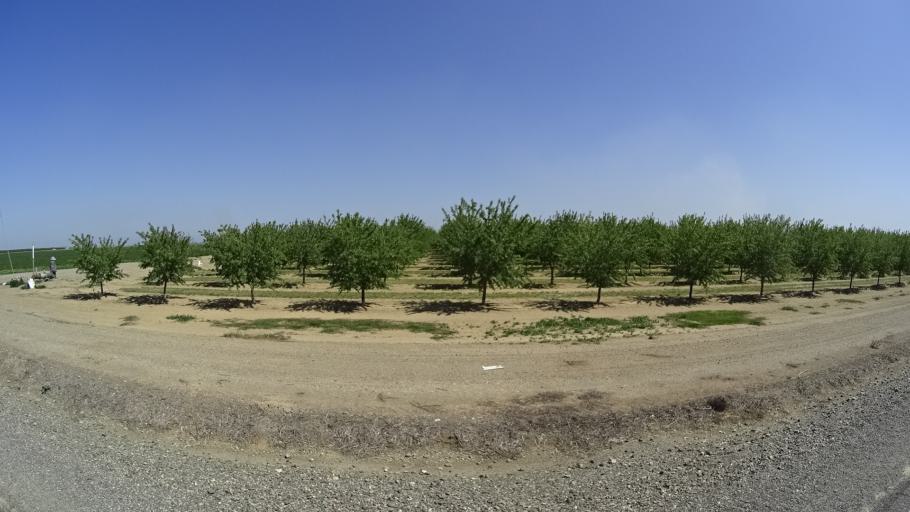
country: US
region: California
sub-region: Glenn County
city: Willows
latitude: 39.5744
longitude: -122.1370
